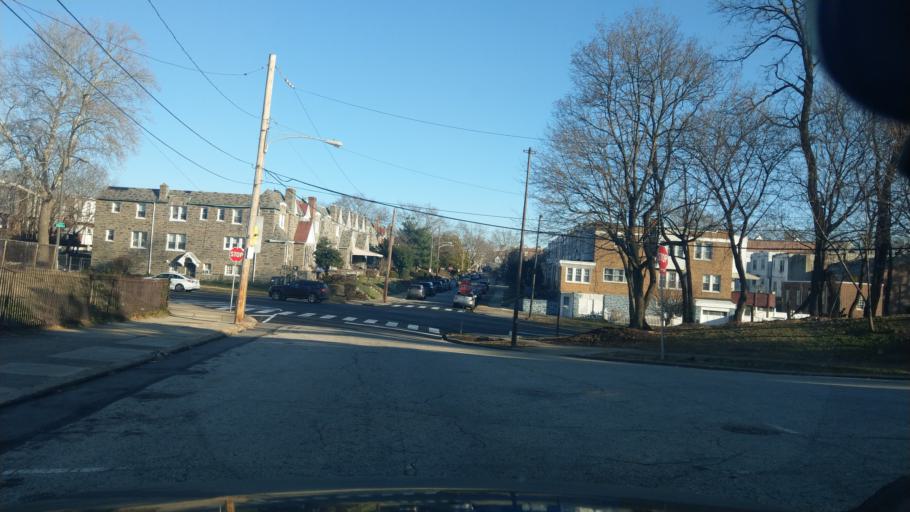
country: US
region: Pennsylvania
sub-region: Montgomery County
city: Wyncote
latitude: 40.0430
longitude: -75.1506
